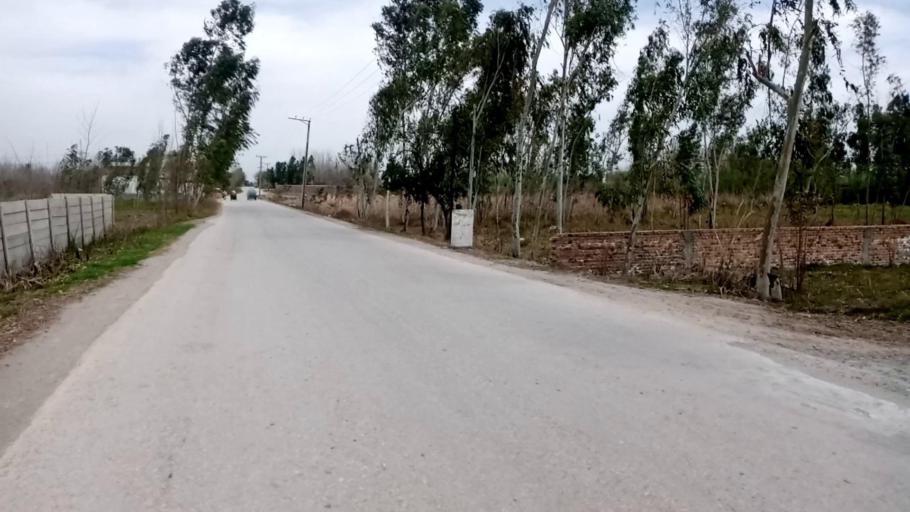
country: PK
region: Khyber Pakhtunkhwa
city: Charsadda
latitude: 34.0627
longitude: 71.6835
